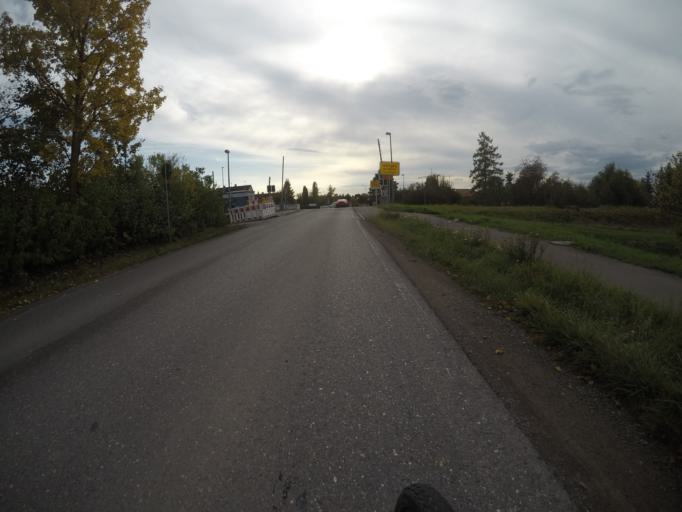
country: DE
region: Baden-Wuerttemberg
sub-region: Regierungsbezirk Stuttgart
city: Herrenberg
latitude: 48.5632
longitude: 8.9074
